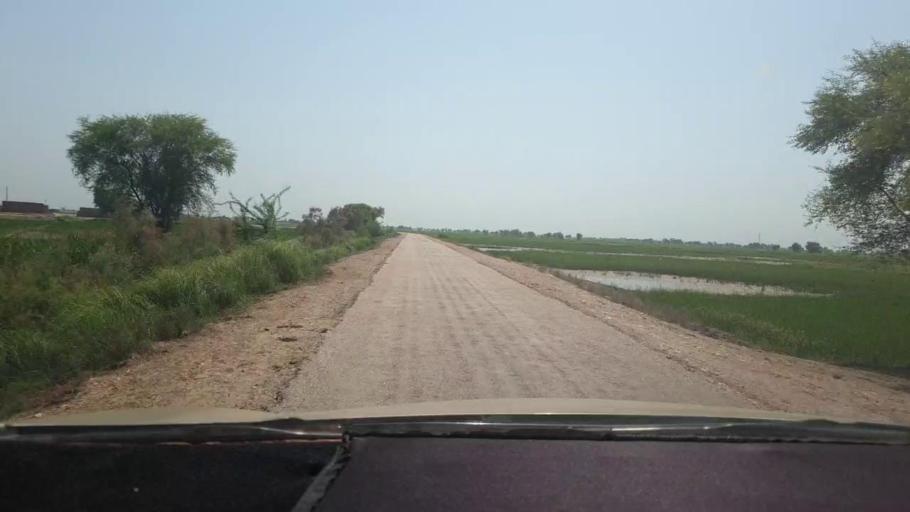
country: PK
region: Sindh
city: Miro Khan
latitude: 27.6766
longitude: 68.0948
